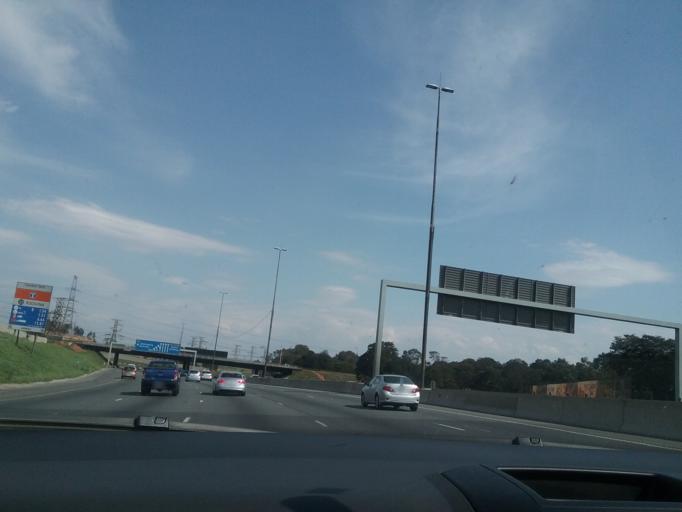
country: ZA
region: Gauteng
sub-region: Ekurhuleni Metropolitan Municipality
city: Germiston
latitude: -26.2011
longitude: 28.1339
